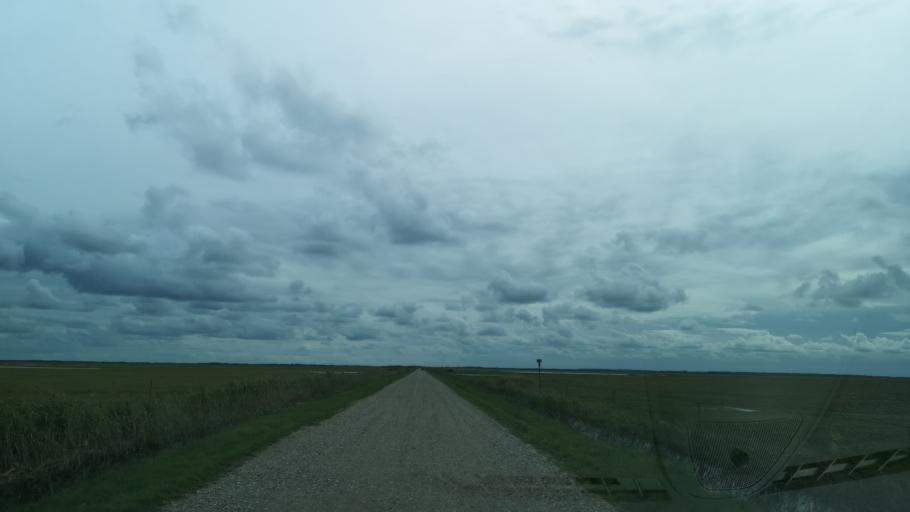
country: DK
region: Central Jutland
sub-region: Ringkobing-Skjern Kommune
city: Hvide Sande
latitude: 55.8905
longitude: 8.2165
